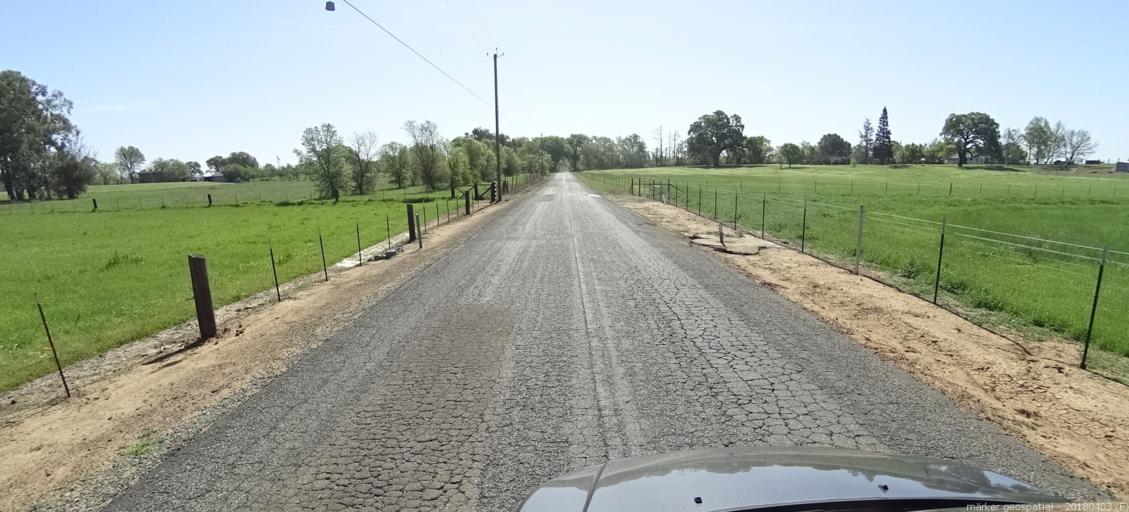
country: US
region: California
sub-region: Sacramento County
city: Wilton
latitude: 38.4352
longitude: -121.2239
